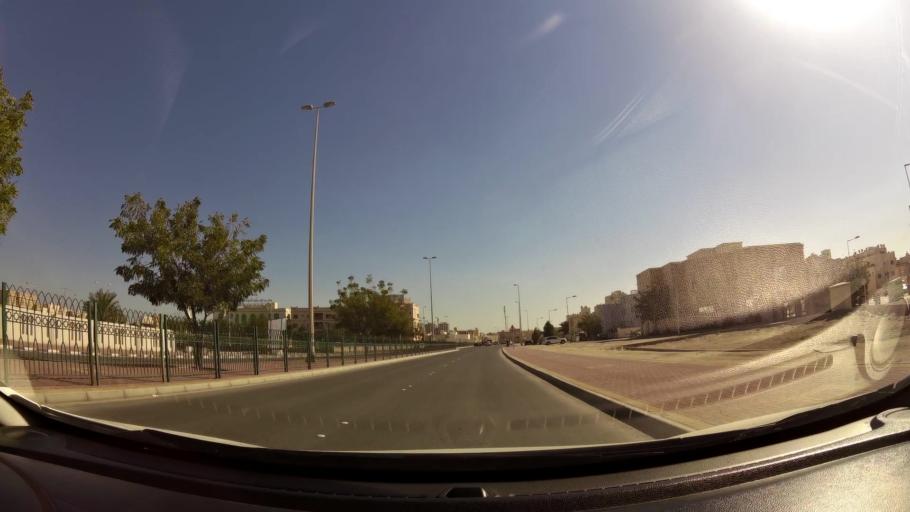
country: BH
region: Muharraq
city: Al Hadd
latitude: 26.2361
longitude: 50.6519
